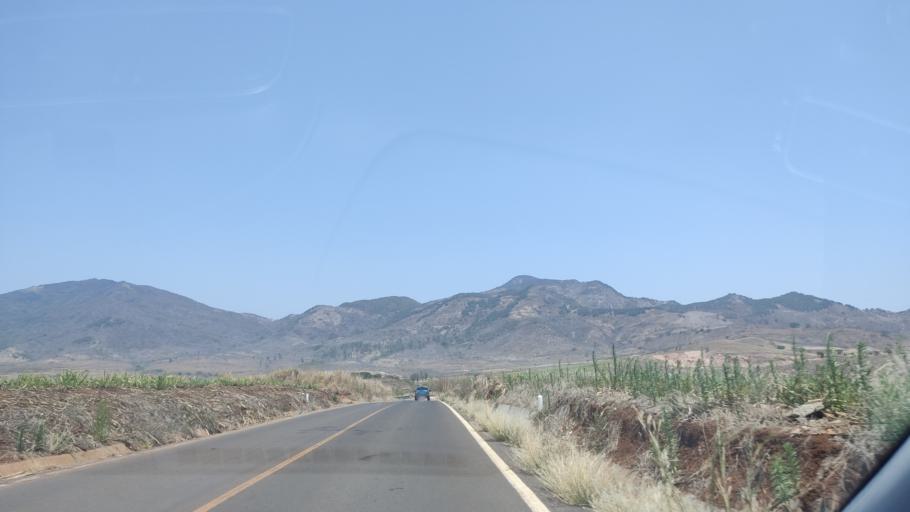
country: MX
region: Nayarit
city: Puga
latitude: 21.6031
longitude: -104.7389
